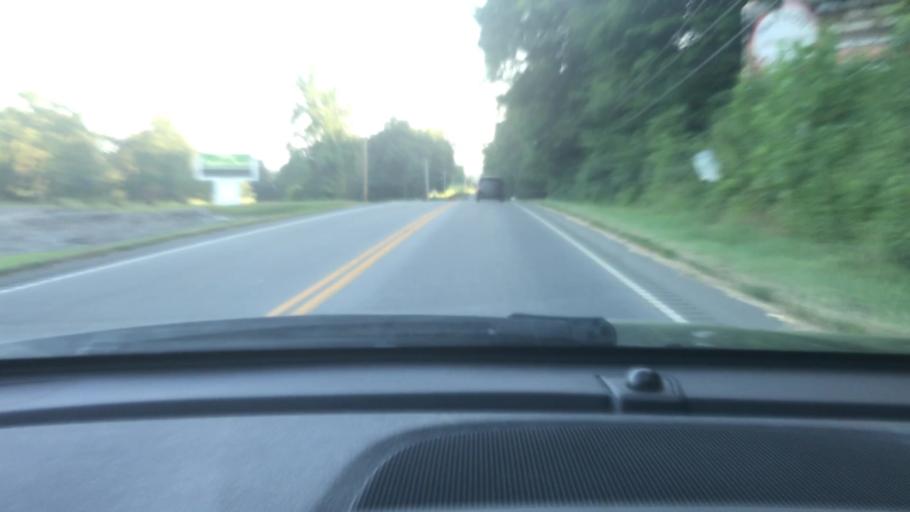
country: US
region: Tennessee
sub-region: Dickson County
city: Dickson
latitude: 36.1011
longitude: -87.3745
